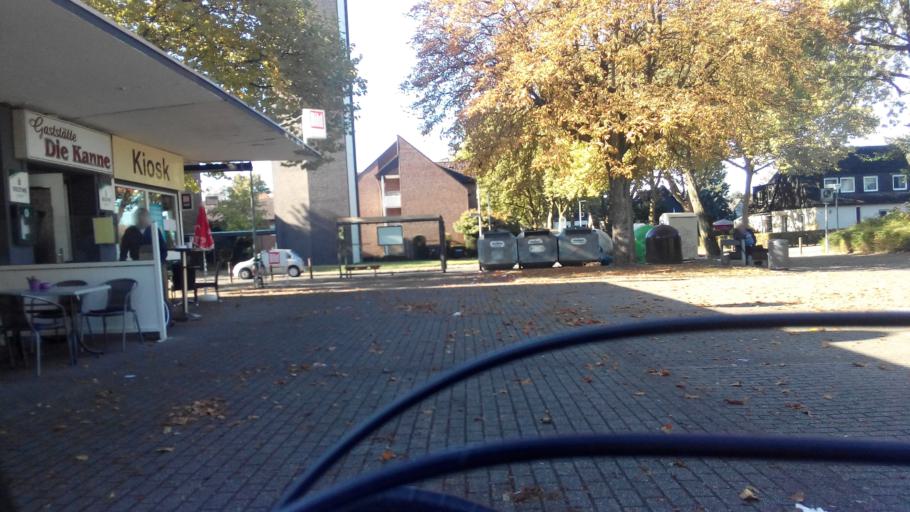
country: DE
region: North Rhine-Westphalia
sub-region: Regierungsbezirk Munster
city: Gelsenkirchen
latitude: 51.4980
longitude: 7.1329
